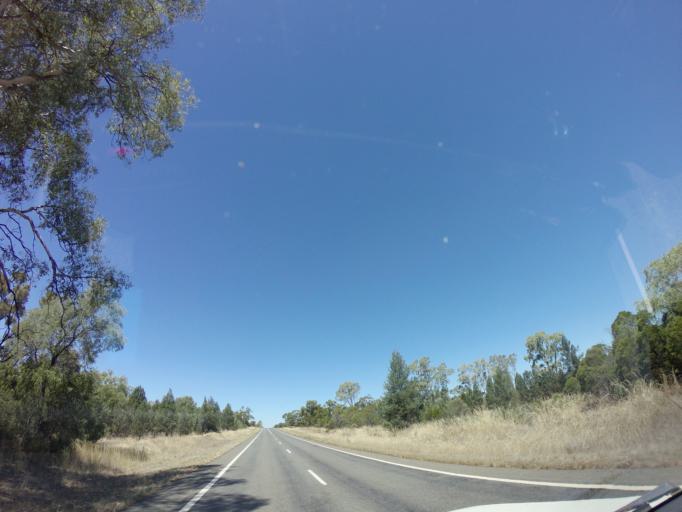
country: AU
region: New South Wales
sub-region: Bogan
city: Nyngan
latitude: -31.5485
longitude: 146.7049
